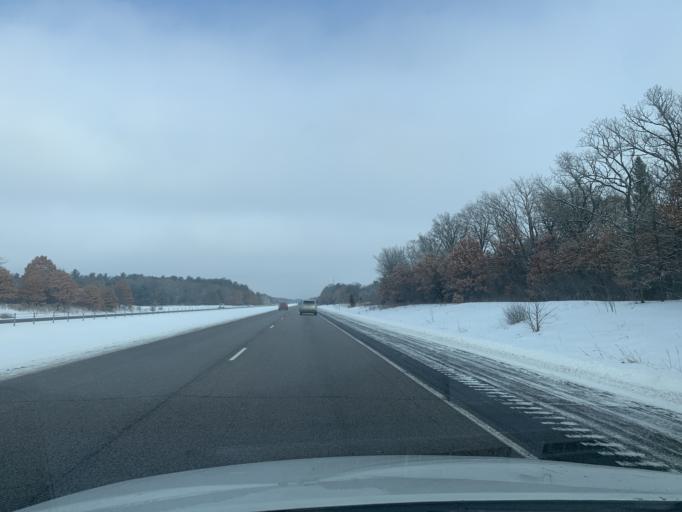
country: US
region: Minnesota
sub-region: Chisago County
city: Wyoming
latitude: 45.3620
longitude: -92.9966
